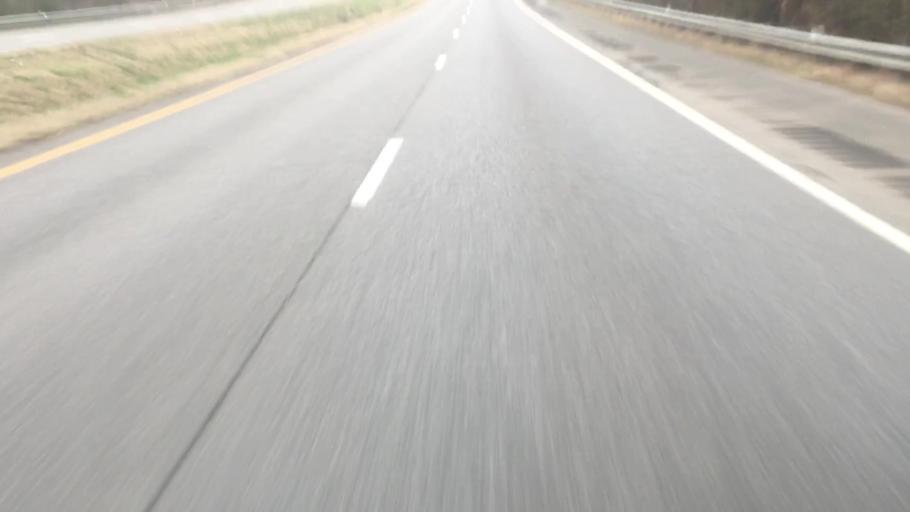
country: US
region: Alabama
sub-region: Jefferson County
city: Graysville
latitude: 33.6833
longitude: -86.9744
